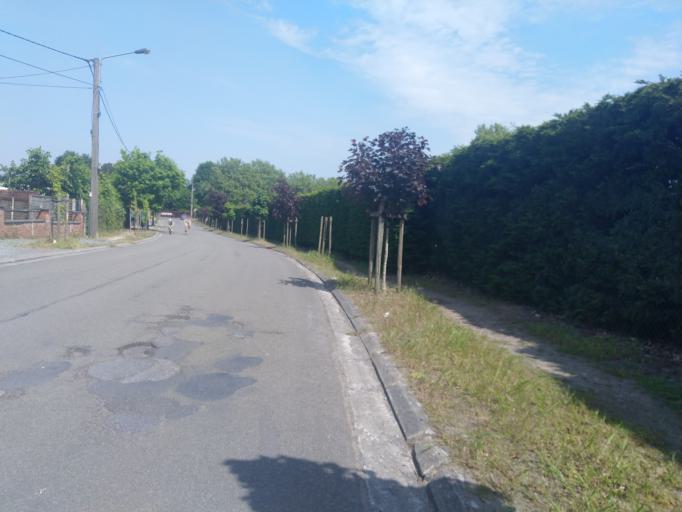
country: BE
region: Wallonia
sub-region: Province du Hainaut
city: Mons
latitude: 50.4628
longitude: 3.9844
